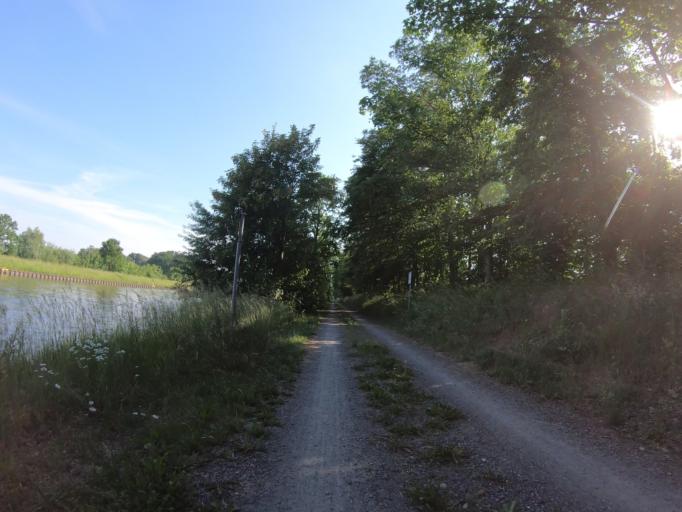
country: DE
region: Lower Saxony
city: Calberlah
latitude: 52.4049
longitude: 10.6170
